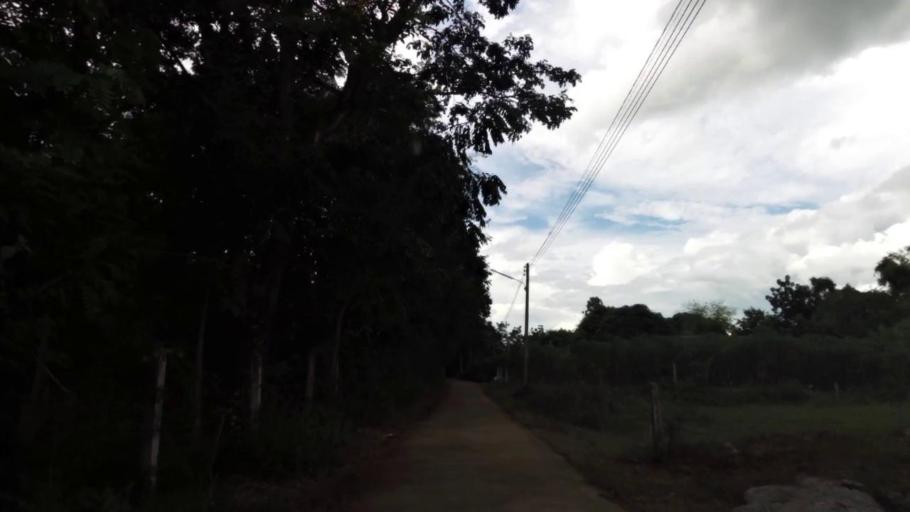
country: TH
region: Nakhon Sawan
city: Phai Sali
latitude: 15.6046
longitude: 100.6678
